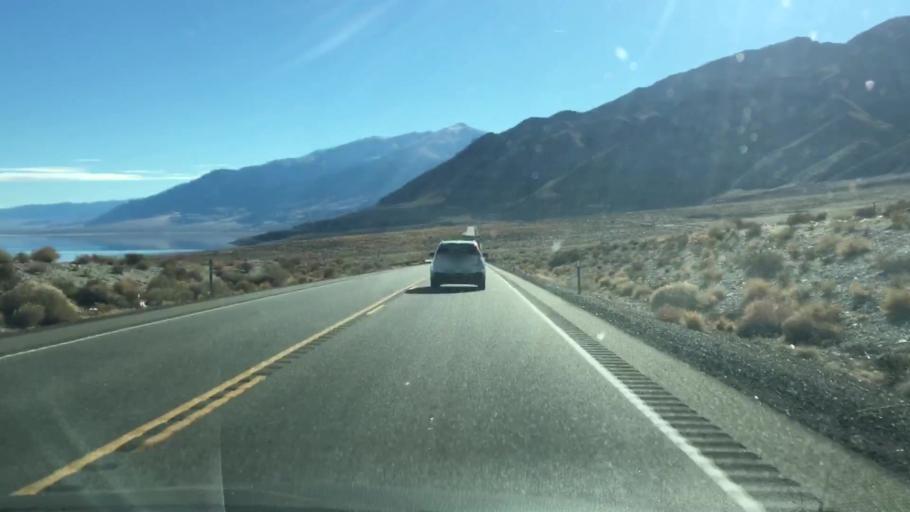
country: US
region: Nevada
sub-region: Mineral County
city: Hawthorne
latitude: 38.7453
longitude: -118.7671
